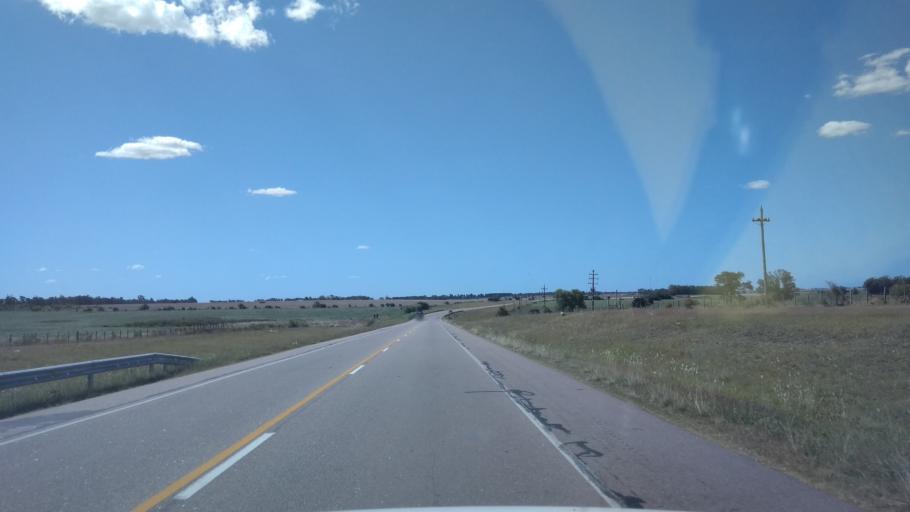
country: UY
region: Florida
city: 25 de Mayo
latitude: -34.2352
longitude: -56.2131
